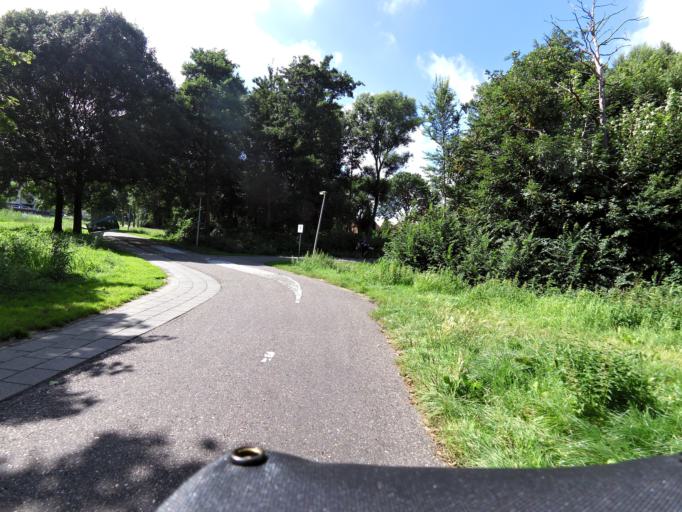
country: NL
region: South Holland
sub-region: Gemeente Spijkenisse
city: Spijkenisse
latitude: 51.8429
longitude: 4.3196
